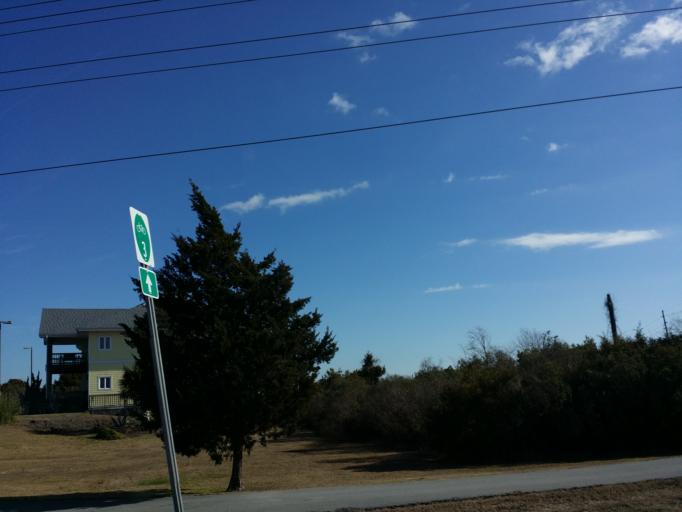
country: US
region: North Carolina
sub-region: Onslow County
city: Sneads Ferry
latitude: 34.4926
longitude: -77.4262
